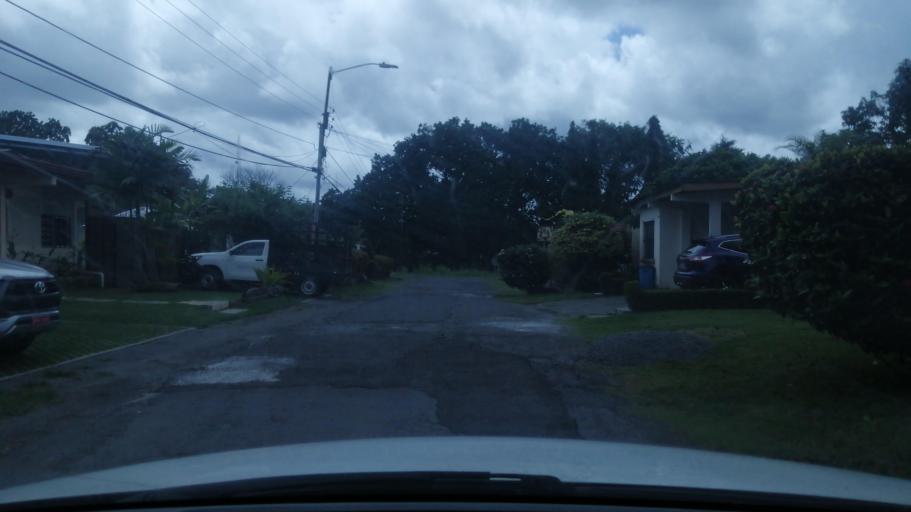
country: PA
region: Chiriqui
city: David
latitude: 8.4420
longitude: -82.4192
